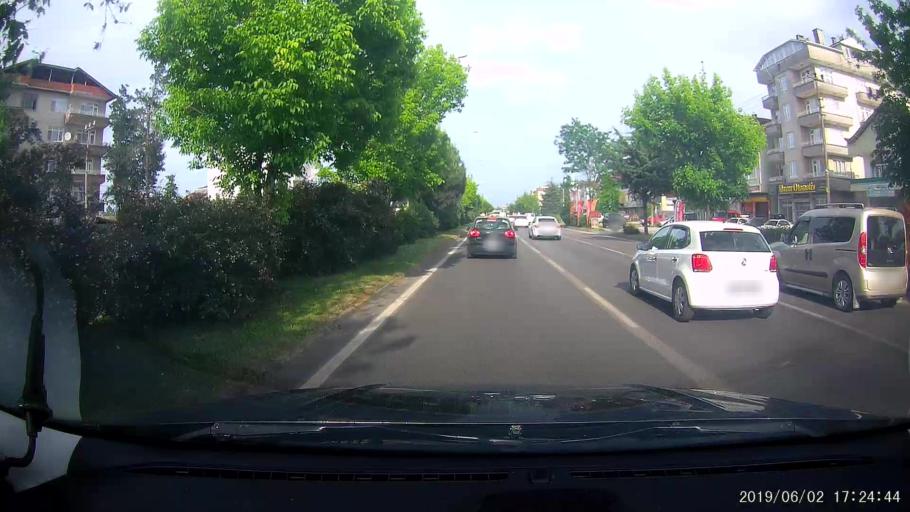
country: TR
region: Samsun
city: Carsamba
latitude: 41.2052
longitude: 36.7063
